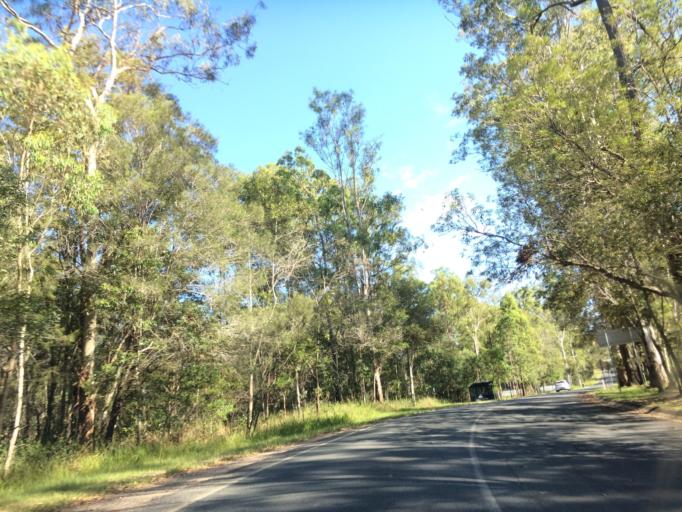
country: AU
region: Queensland
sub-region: Ipswich
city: Springfield Lakes
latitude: -27.7102
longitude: 152.9571
